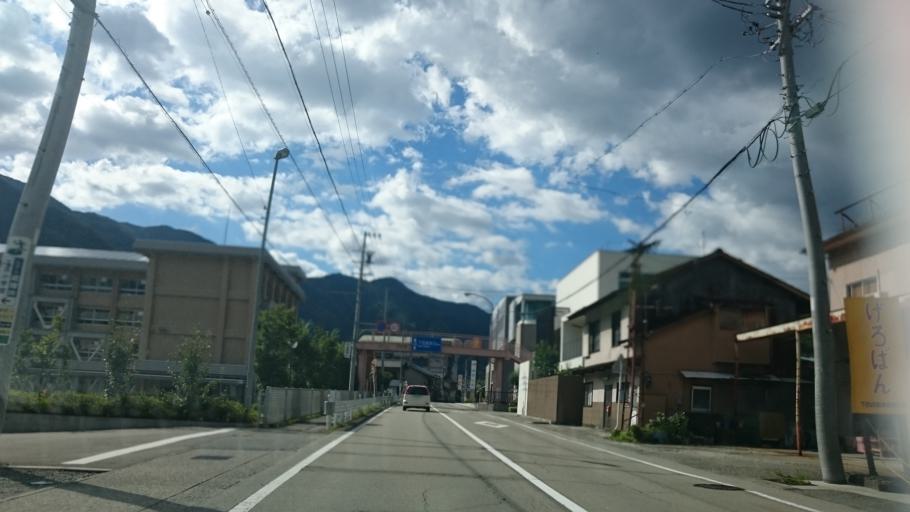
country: JP
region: Gifu
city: Gujo
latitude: 35.8012
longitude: 137.2486
